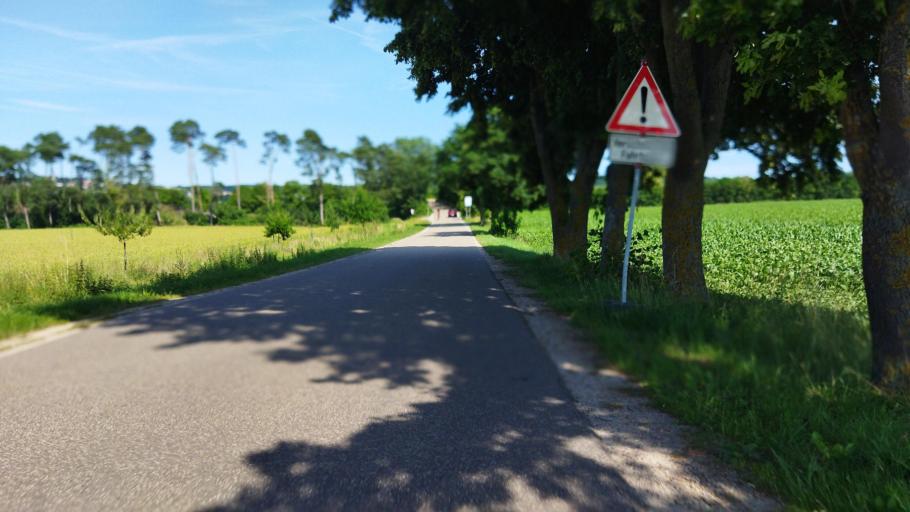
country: DE
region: Bavaria
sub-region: Lower Bavaria
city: Bad Abbach
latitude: 48.9365
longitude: 12.0223
